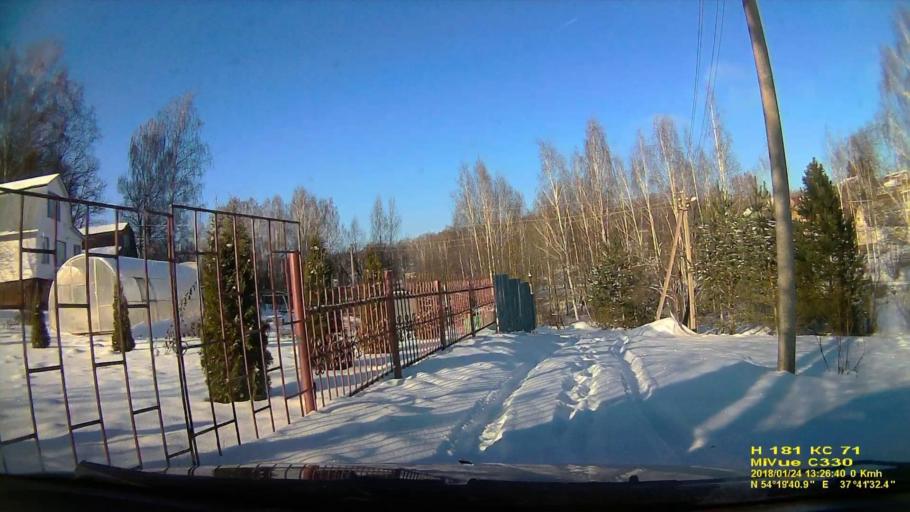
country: RU
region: Tula
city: Revyakino
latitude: 54.3280
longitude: 37.6924
